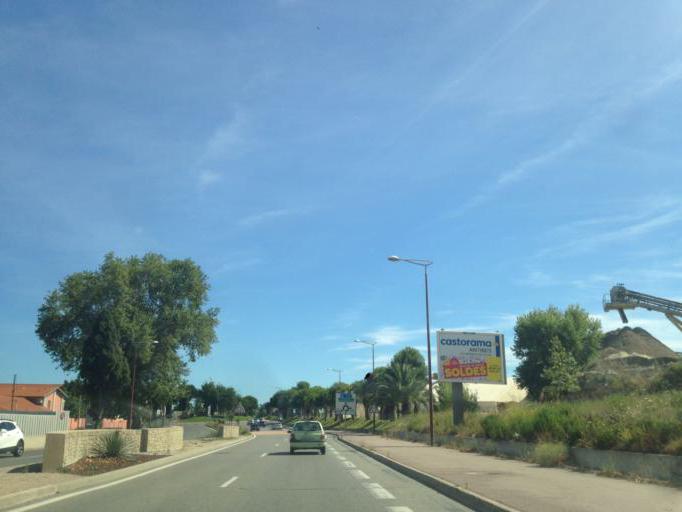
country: FR
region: Provence-Alpes-Cote d'Azur
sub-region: Departement des Alpes-Maritimes
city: Saint-Laurent-du-Var
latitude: 43.6980
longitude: 7.1903
